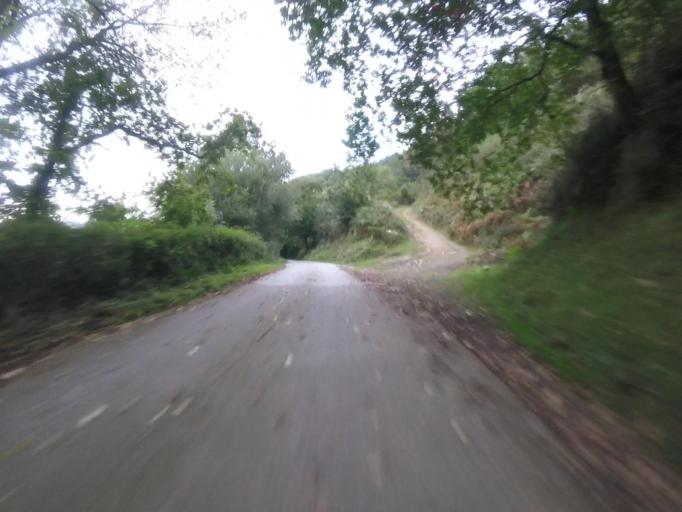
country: ES
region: Basque Country
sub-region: Provincia de Guipuzcoa
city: Errenteria
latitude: 43.2724
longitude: -1.8336
